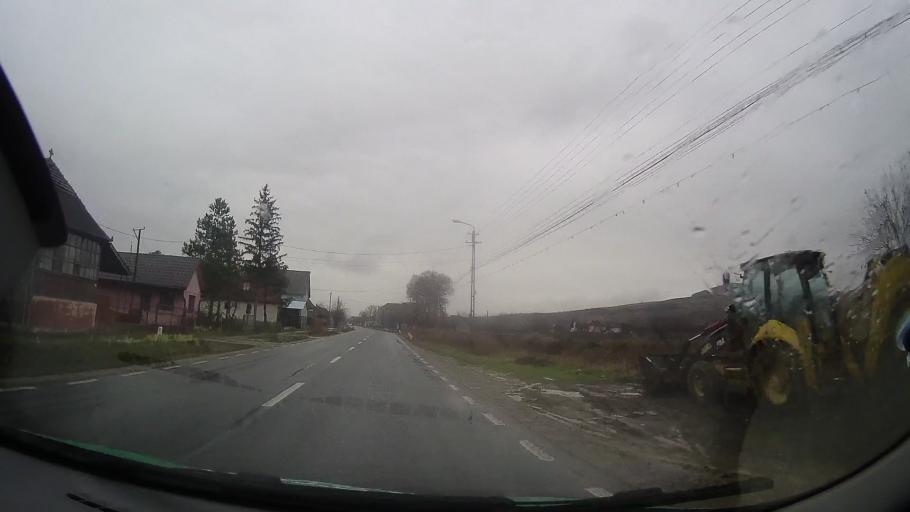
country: RO
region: Bistrita-Nasaud
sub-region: Comuna Galatii Bistritei
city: Galatii Bistritei
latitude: 46.9729
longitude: 24.4331
